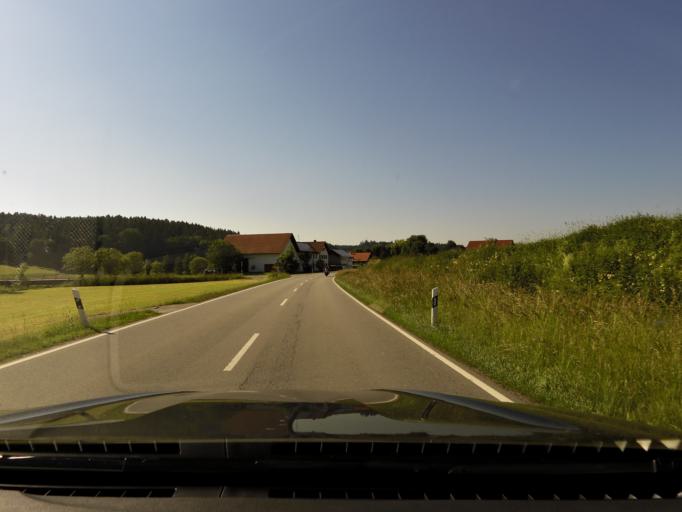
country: DE
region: Bavaria
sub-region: Upper Bavaria
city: Rohrbach
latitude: 48.3037
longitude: 12.5624
